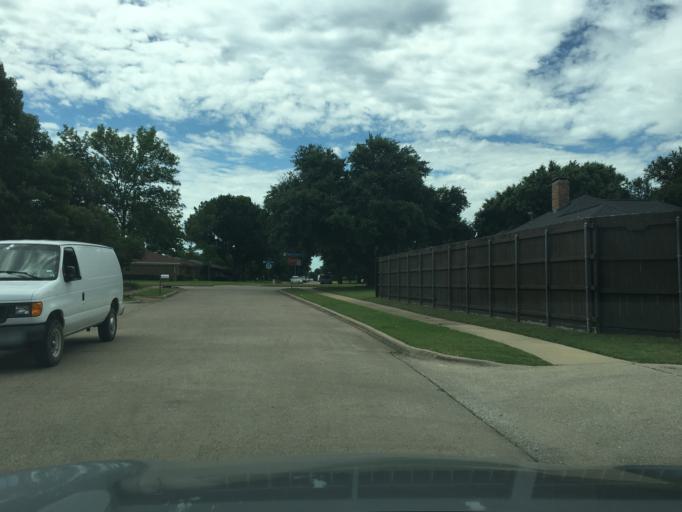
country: US
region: Texas
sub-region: Dallas County
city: Richardson
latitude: 32.9392
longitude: -96.7007
